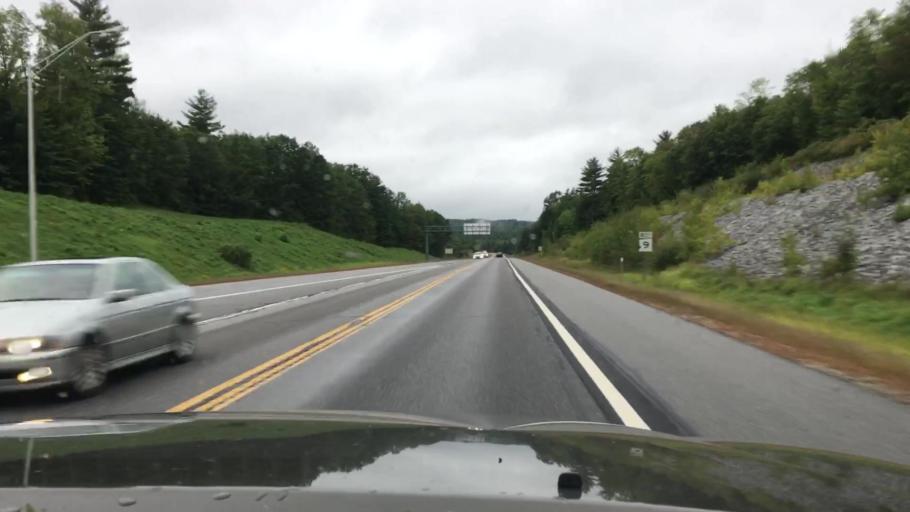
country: US
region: New Hampshire
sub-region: Hillsborough County
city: Hillsborough
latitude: 43.1167
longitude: -71.9234
